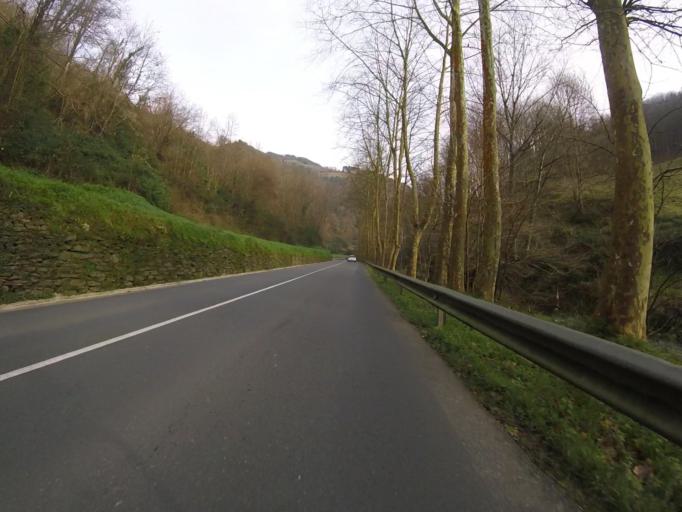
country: ES
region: Basque Country
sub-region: Provincia de Guipuzcoa
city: Belaunza
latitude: 43.1377
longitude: -2.0567
